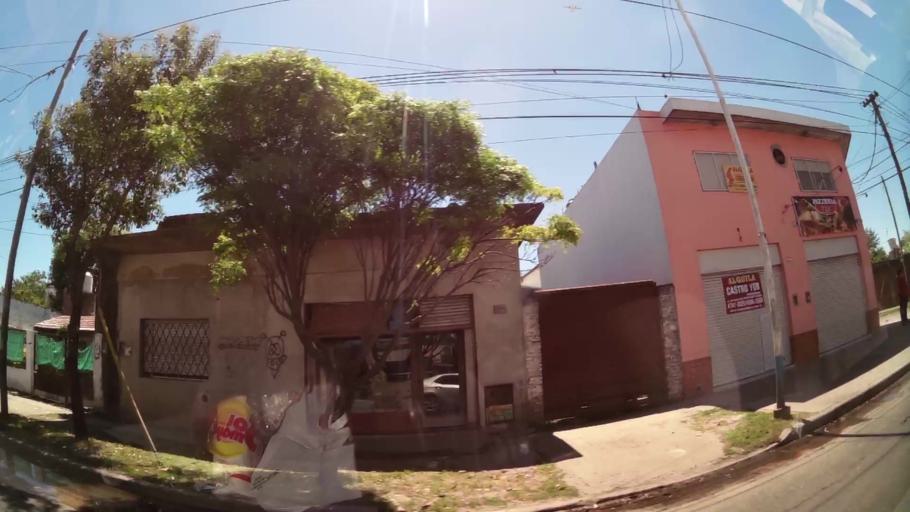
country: AR
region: Buenos Aires
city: Hurlingham
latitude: -34.4926
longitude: -58.6696
